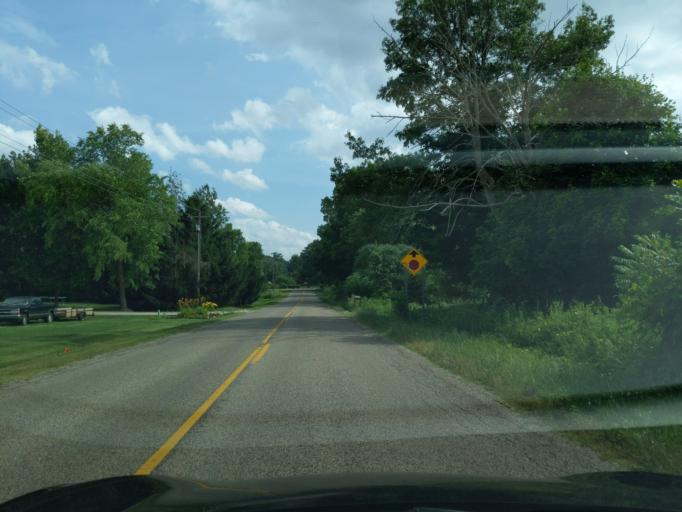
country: US
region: Michigan
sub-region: Eaton County
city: Eaton Rapids
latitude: 42.4965
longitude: -84.6305
